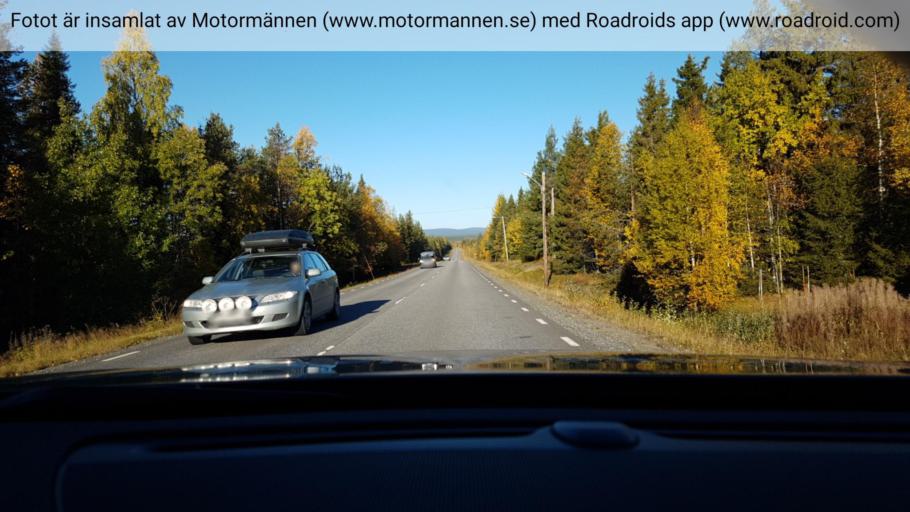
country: SE
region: Vaesterbotten
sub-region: Skelleftea Kommun
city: Storvik
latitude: 65.3621
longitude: 20.4275
